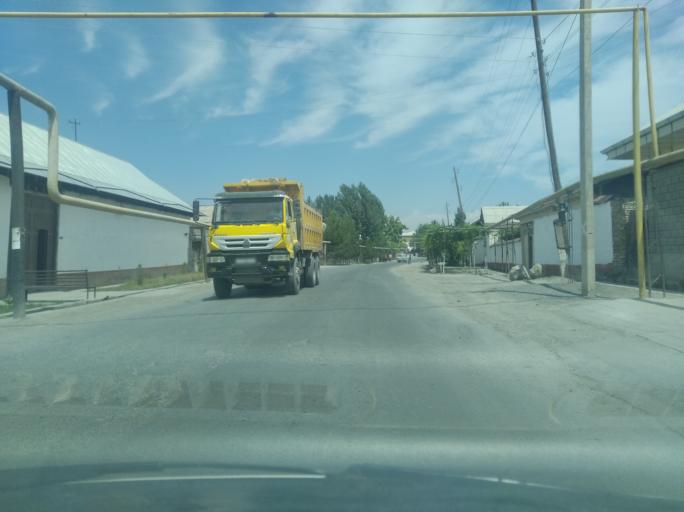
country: UZ
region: Andijon
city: Khujaobod
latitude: 40.6353
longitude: 72.4490
